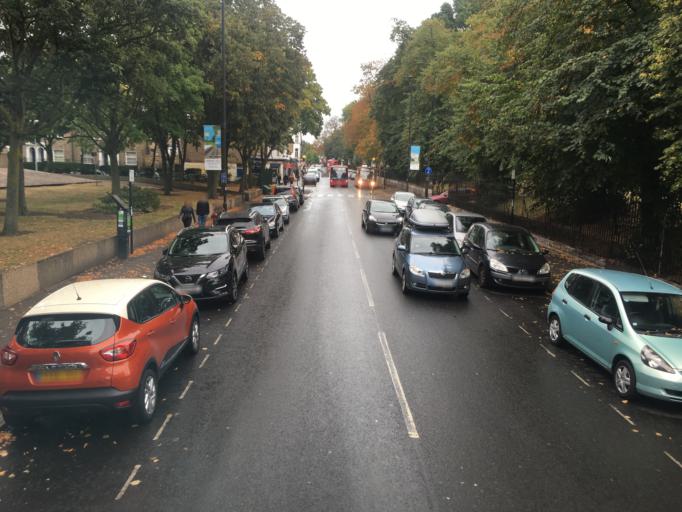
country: GB
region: England
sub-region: Greater London
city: Brixton
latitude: 51.4533
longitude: -0.1054
